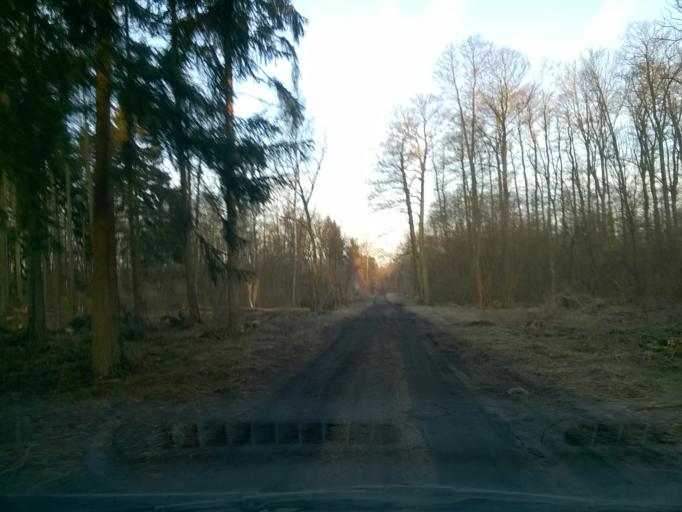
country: PL
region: Kujawsko-Pomorskie
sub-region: Powiat nakielski
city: Sadki
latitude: 53.1211
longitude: 17.4064
